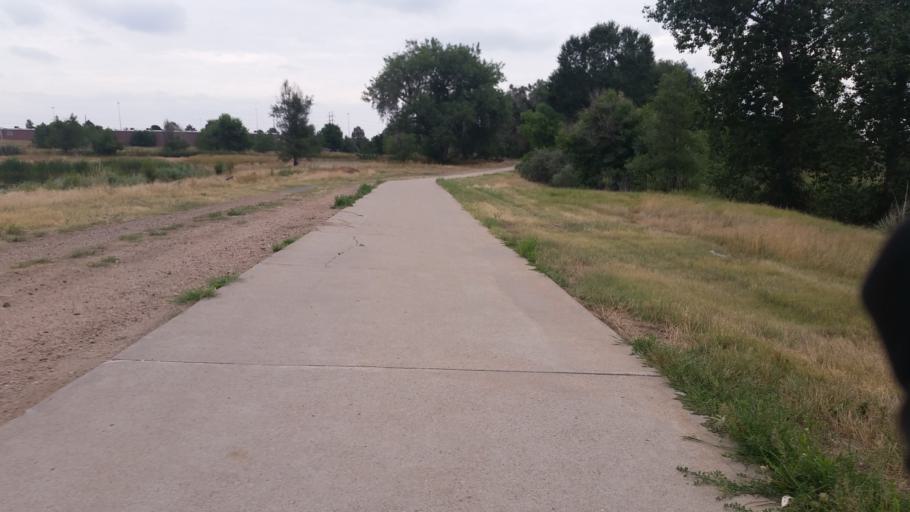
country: US
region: Colorado
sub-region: Adams County
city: Twin Lakes
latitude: 39.8204
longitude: -104.9913
